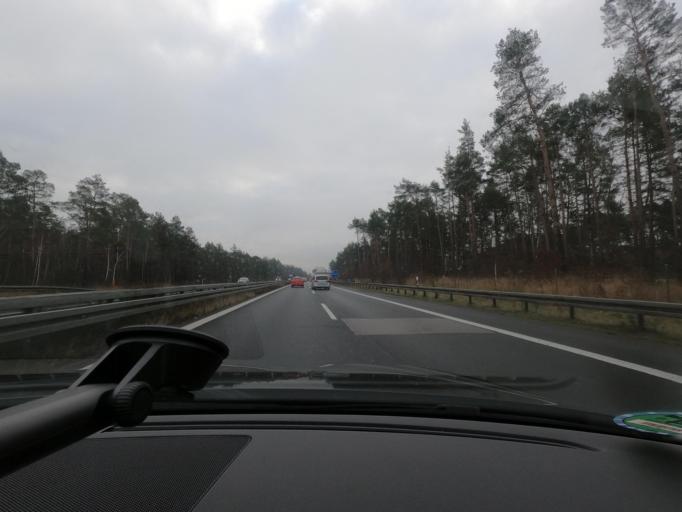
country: DE
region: Bavaria
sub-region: Upper Franconia
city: Gundelsheim
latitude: 49.9182
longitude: 10.9329
